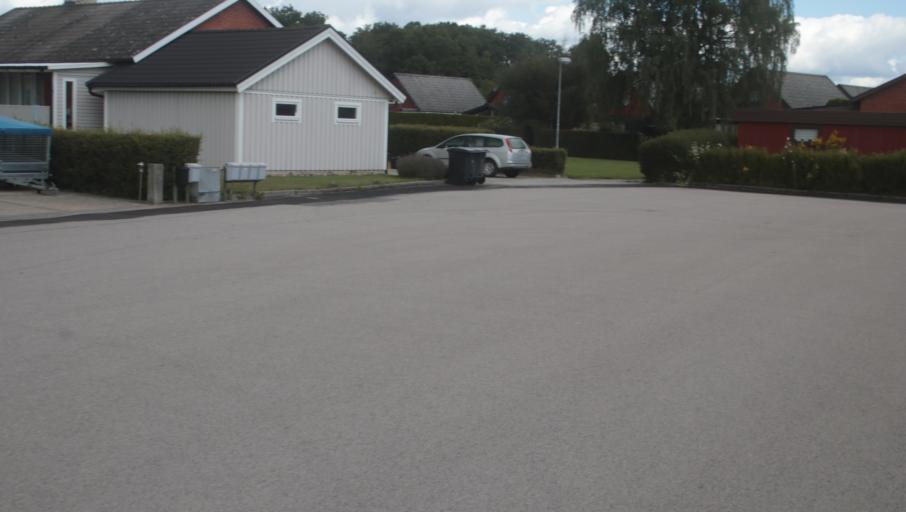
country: SE
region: Blekinge
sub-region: Karlshamns Kommun
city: Morrum
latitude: 56.1946
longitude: 14.7417
